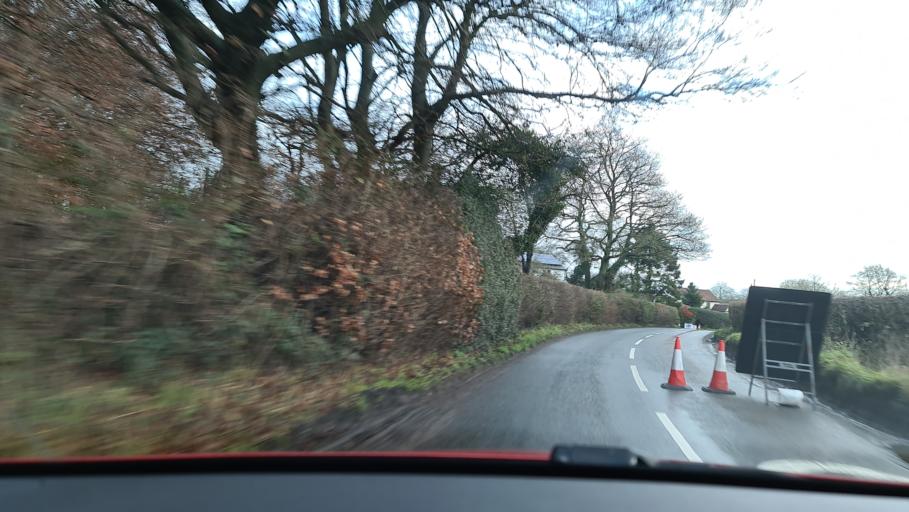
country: GB
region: England
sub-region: Buckinghamshire
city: Wendover
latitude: 51.7418
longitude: -0.7186
